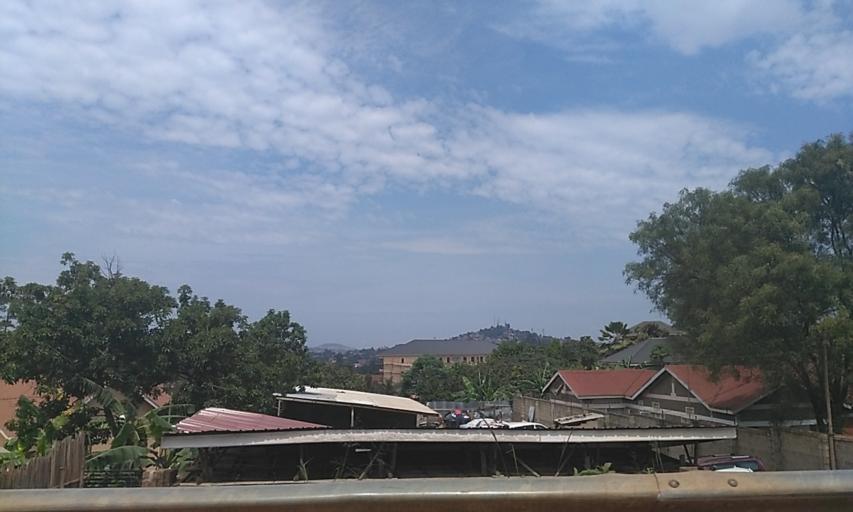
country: UG
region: Central Region
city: Kampala Central Division
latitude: 0.3081
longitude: 32.5544
